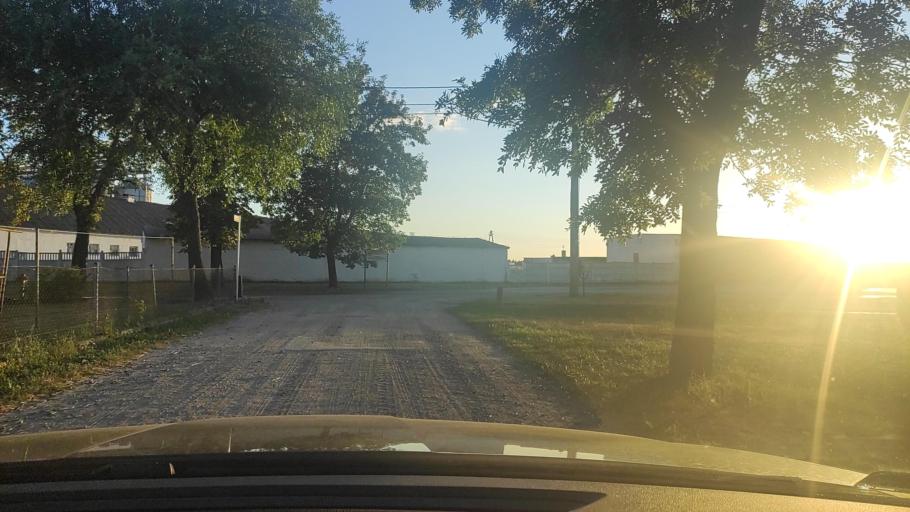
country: PL
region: Greater Poland Voivodeship
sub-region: Powiat poznanski
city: Kobylnica
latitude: 52.4533
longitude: 17.1243
